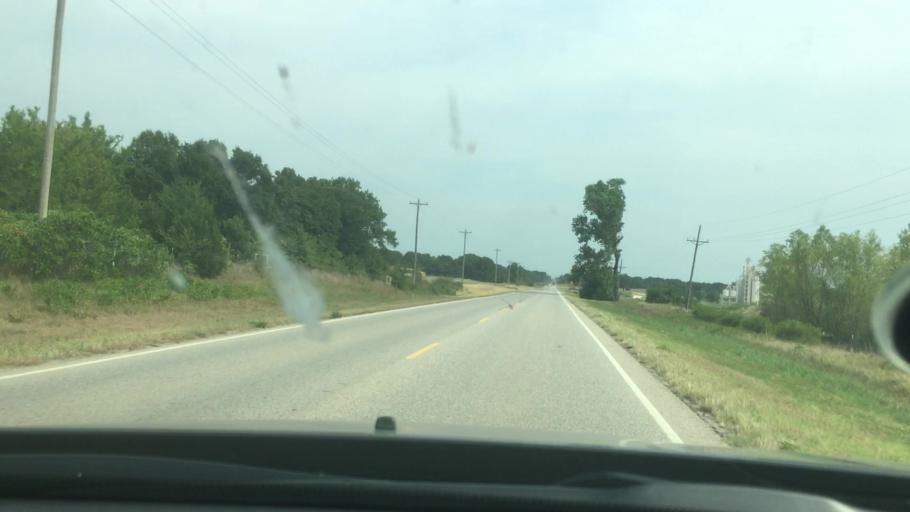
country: US
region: Oklahoma
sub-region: Bryan County
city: Durant
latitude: 34.2090
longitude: -96.4250
